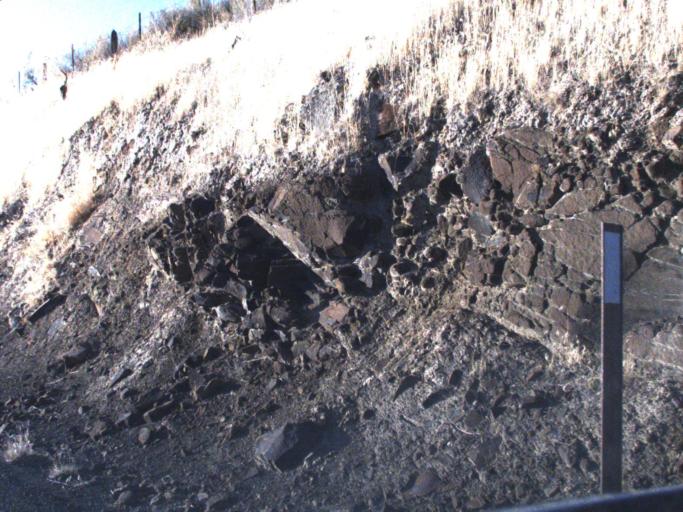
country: US
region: Washington
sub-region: Adams County
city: Ritzville
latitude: 46.6990
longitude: -118.4069
